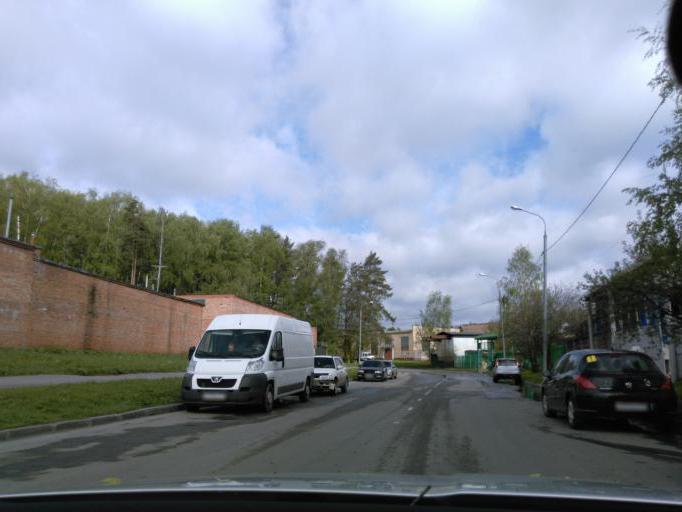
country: RU
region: Moscow
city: Zelenograd
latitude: 56.0046
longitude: 37.1858
